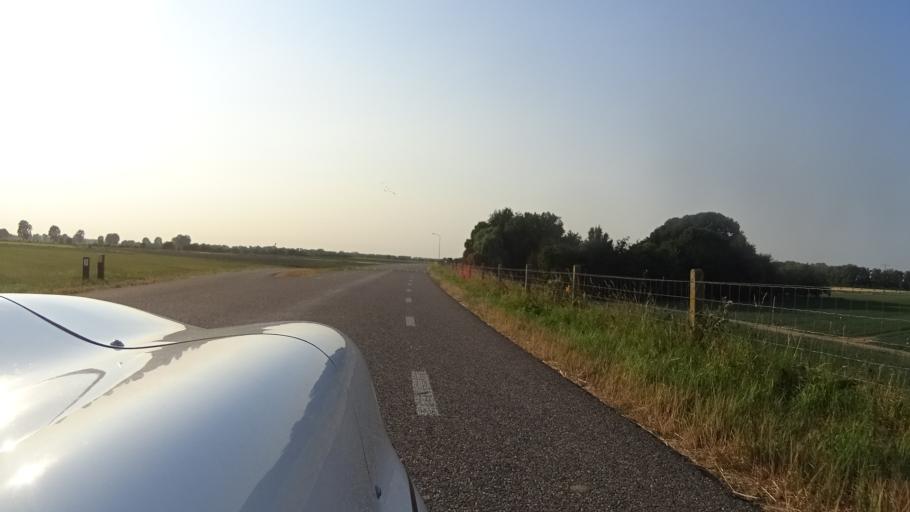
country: NL
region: Gelderland
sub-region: Gemeente Wijchen
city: Bergharen
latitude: 51.8132
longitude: 5.6569
